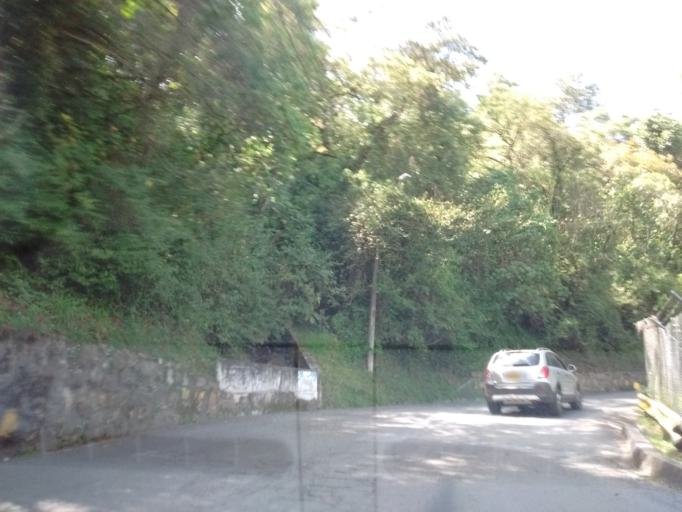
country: CO
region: Antioquia
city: Medellin
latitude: 6.2399
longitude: -75.5142
